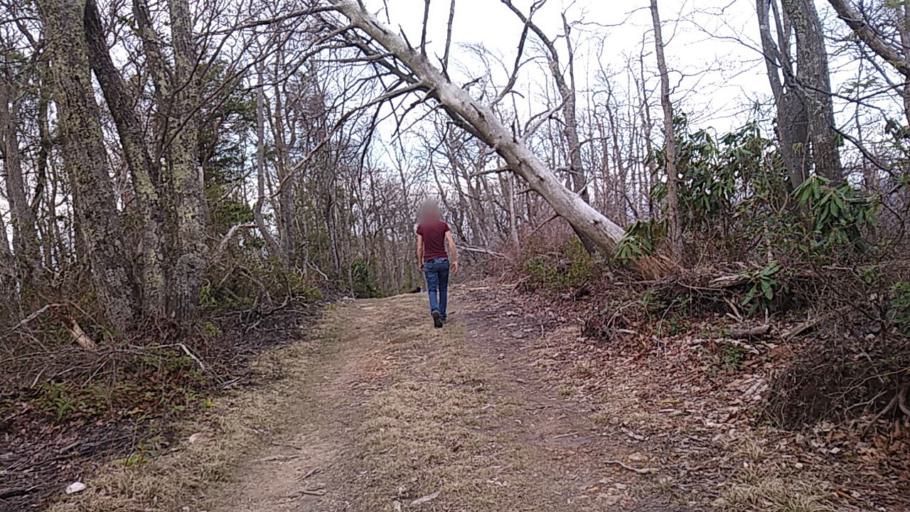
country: US
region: Tennessee
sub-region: Greene County
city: Tusculum
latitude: 36.0627
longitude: -82.6760
